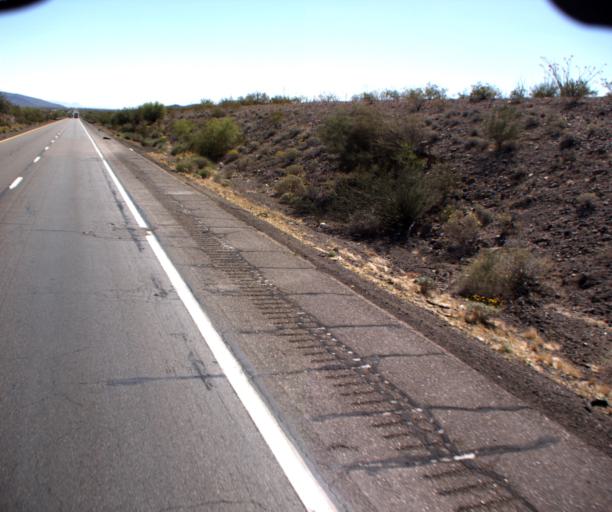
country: US
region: Arizona
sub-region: La Paz County
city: Quartzsite
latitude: 33.6604
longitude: -114.0020
